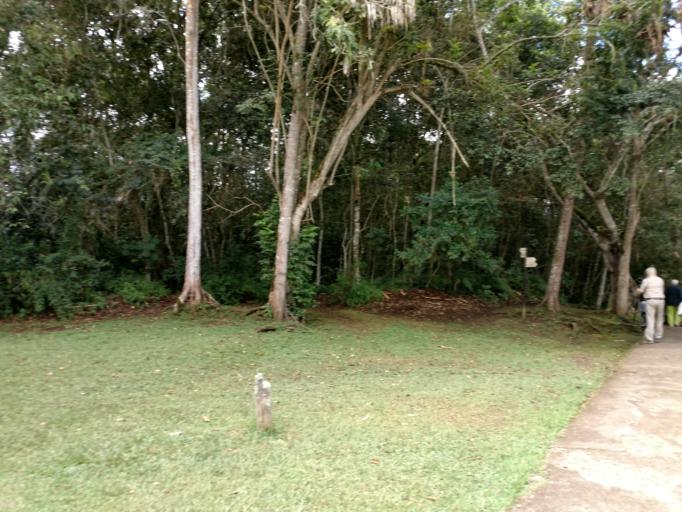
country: CO
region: Huila
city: San Agustin
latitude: 1.8806
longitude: -76.2983
